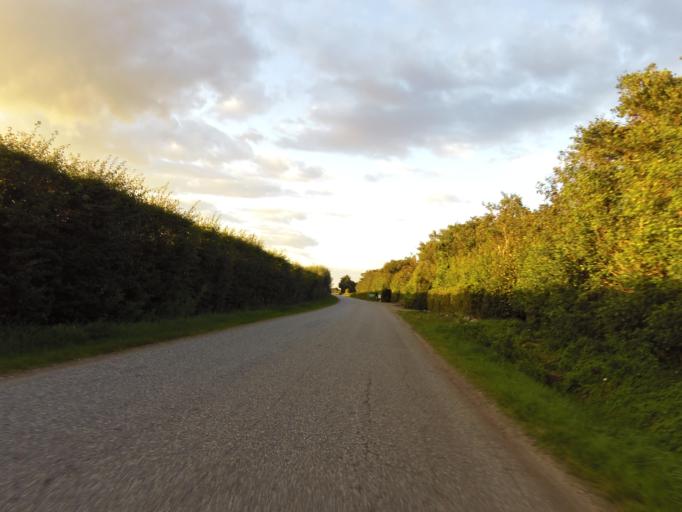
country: DK
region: South Denmark
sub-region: Tonder Kommune
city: Sherrebek
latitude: 55.2428
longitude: 8.8912
